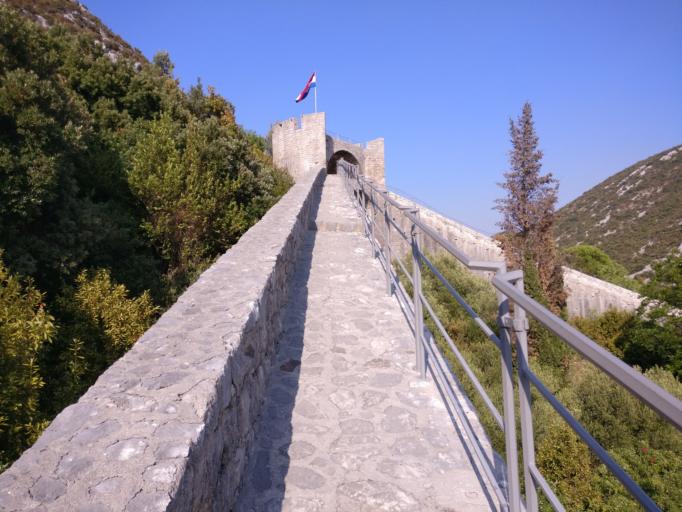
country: HR
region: Dubrovacko-Neretvanska
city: Ston
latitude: 42.8401
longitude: 17.6951
